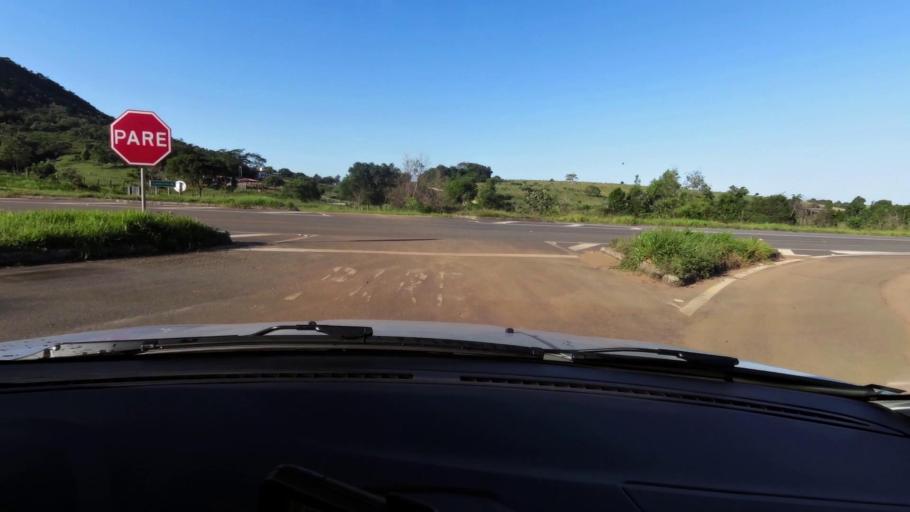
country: BR
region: Espirito Santo
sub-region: Guarapari
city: Guarapari
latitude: -20.7213
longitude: -40.5733
